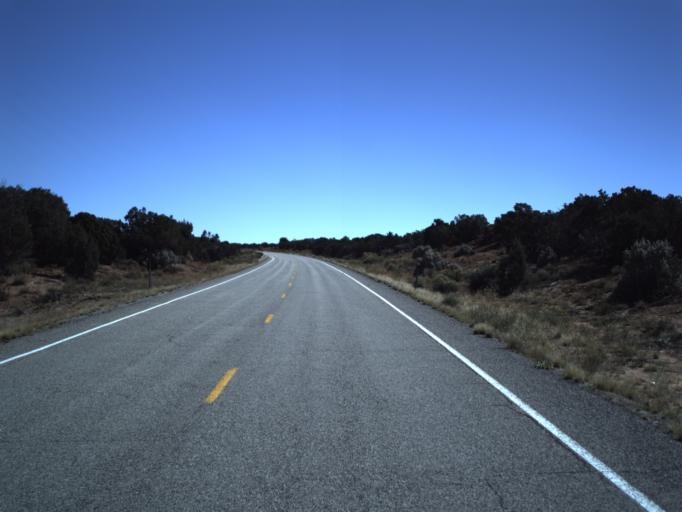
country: US
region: Utah
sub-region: San Juan County
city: Blanding
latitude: 37.5433
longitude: -109.9793
